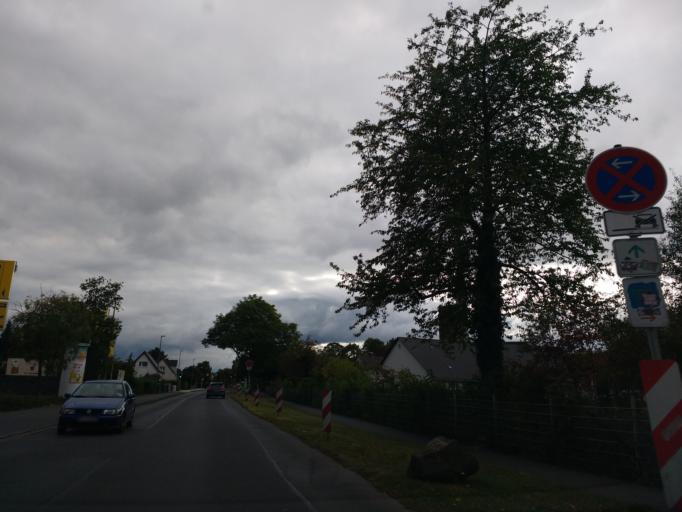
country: DE
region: Hesse
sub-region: Regierungsbezirk Kassel
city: Lohfelden
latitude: 51.2922
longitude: 9.5418
